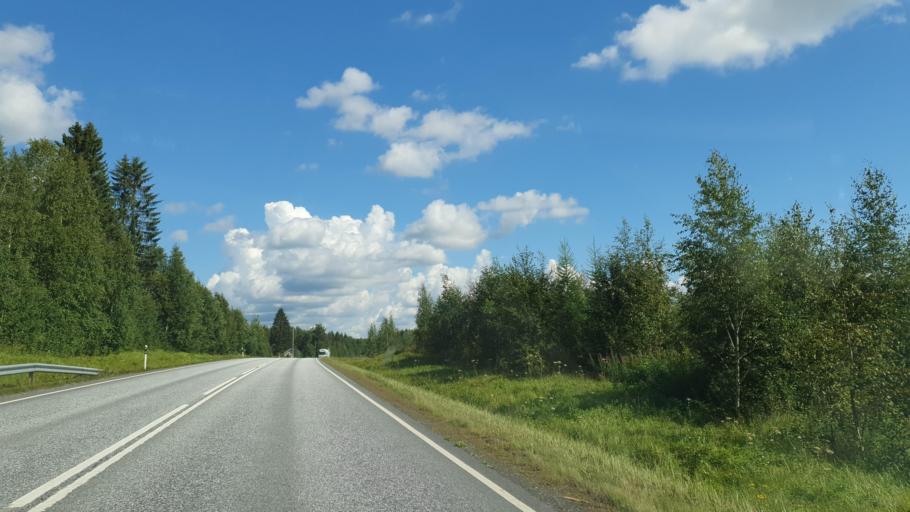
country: FI
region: Northern Savo
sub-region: Ylae-Savo
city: Sonkajaervi
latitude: 63.7570
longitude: 27.3942
